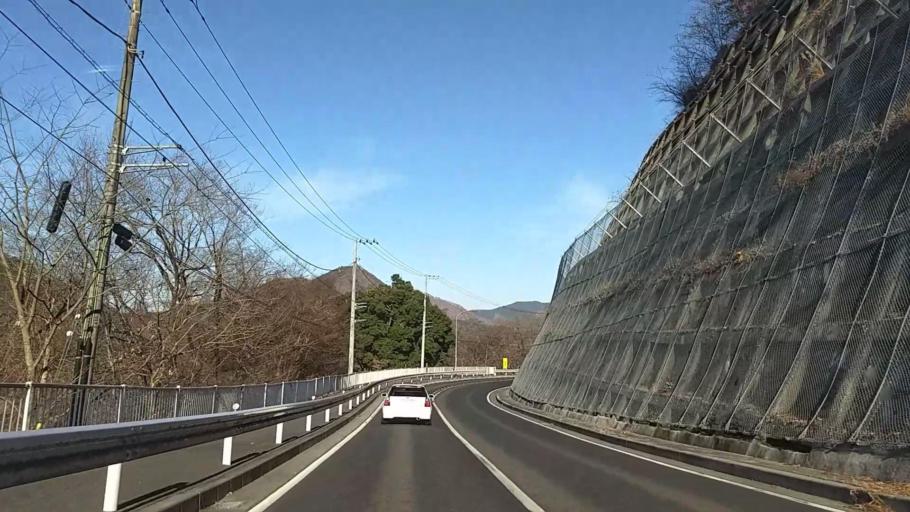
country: JP
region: Yamanashi
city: Uenohara
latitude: 35.5488
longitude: 139.1496
